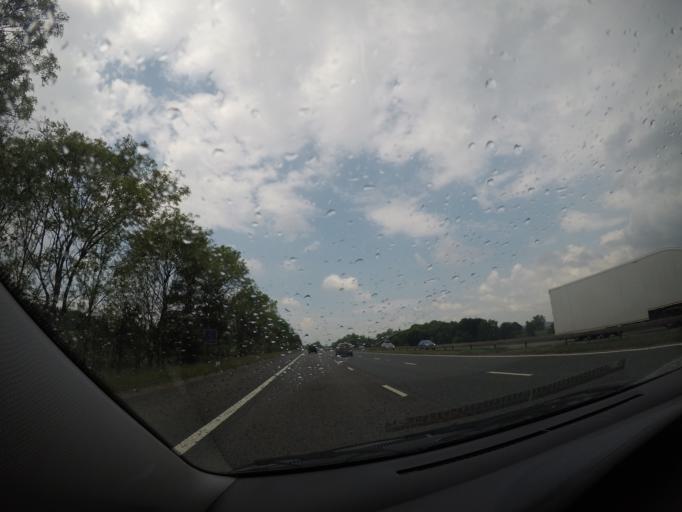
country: GB
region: England
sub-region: Cumbria
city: Penrith
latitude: 54.7410
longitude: -2.8089
